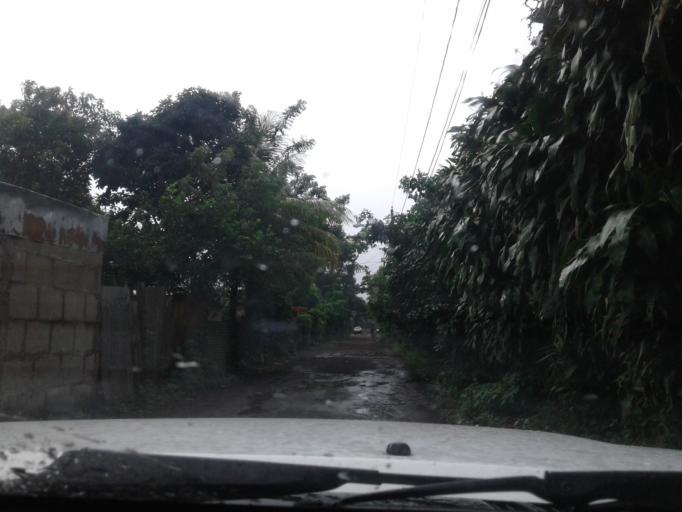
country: NI
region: Carazo
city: San Marcos
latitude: 11.8988
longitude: -86.2023
